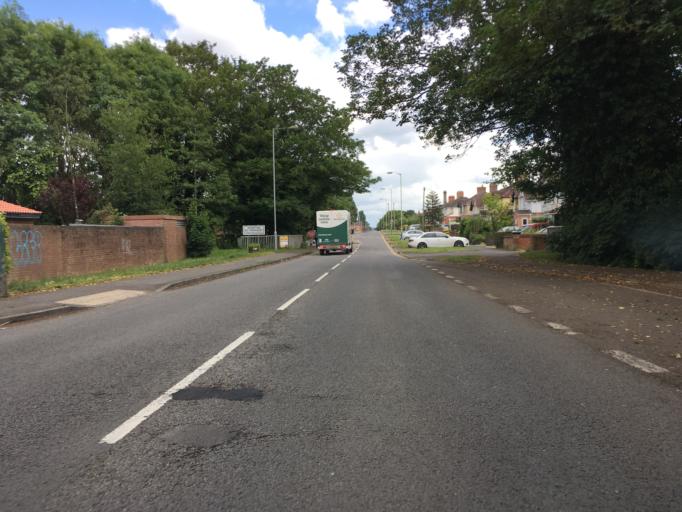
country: GB
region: England
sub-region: Borough of Swindon
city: Broad Blunsdon
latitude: 51.5953
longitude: -1.7666
